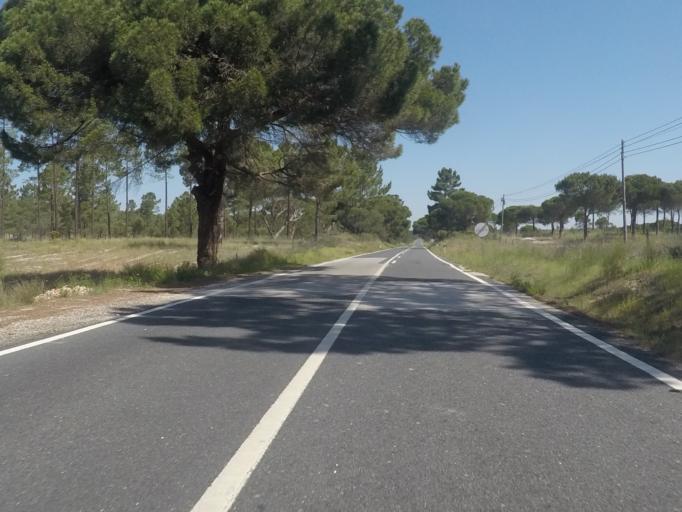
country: PT
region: Setubal
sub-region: Grandola
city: Grandola
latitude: 38.2852
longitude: -8.7262
